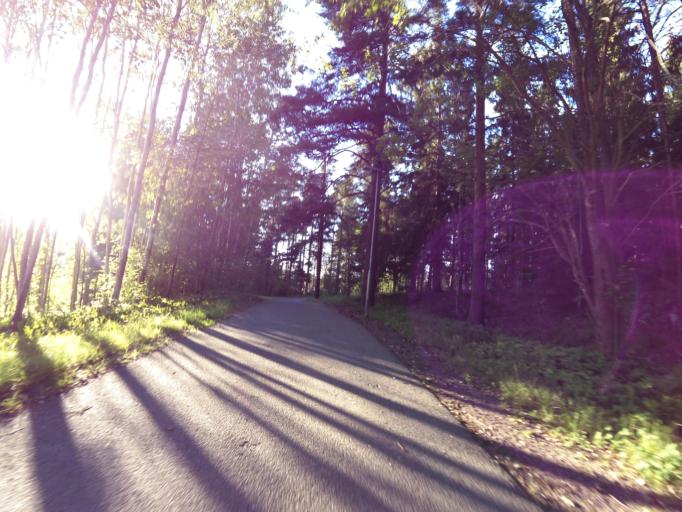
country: SE
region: Gaevleborg
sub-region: Gavle Kommun
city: Gavle
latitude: 60.6566
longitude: 17.1413
